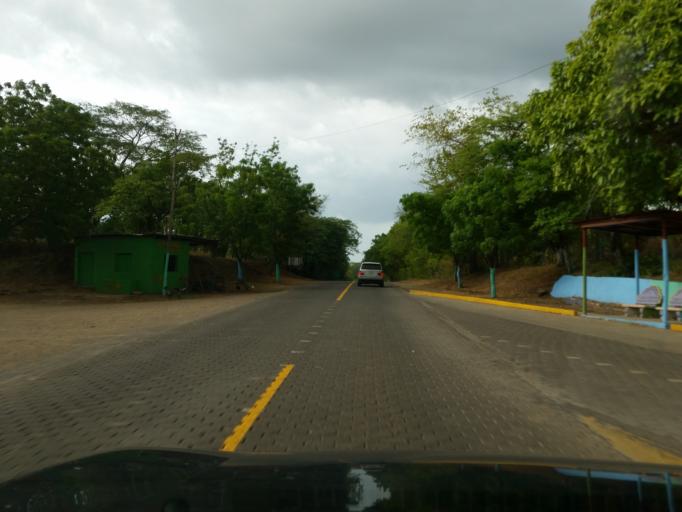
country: NI
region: Managua
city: Carlos Fonseca Amador
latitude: 11.9834
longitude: -86.5153
